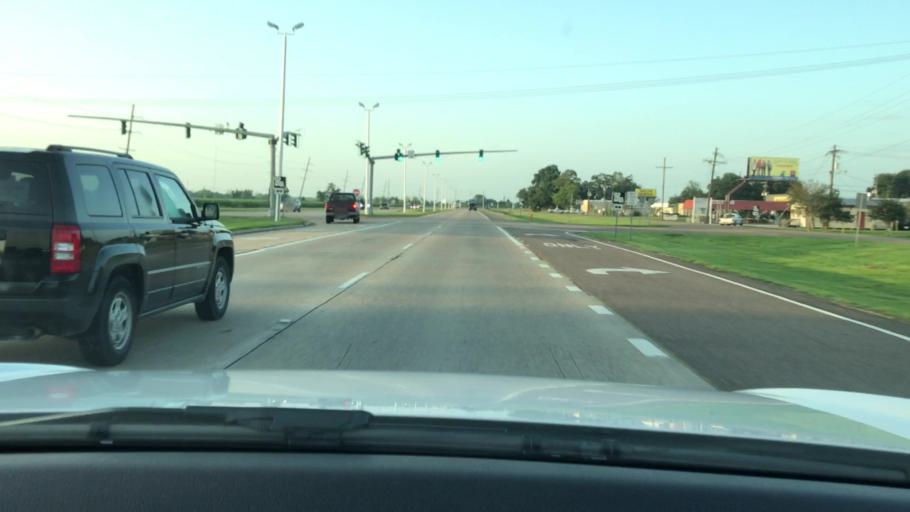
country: US
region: Louisiana
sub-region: West Baton Rouge Parish
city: Addis
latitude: 30.3563
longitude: -91.2597
